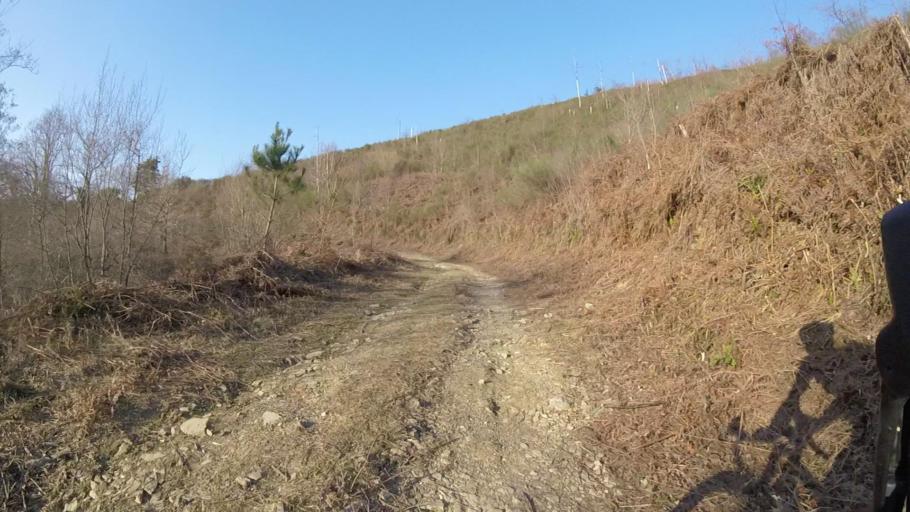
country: ES
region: Navarre
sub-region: Provincia de Navarra
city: Arano
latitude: 43.2224
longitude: -1.8633
